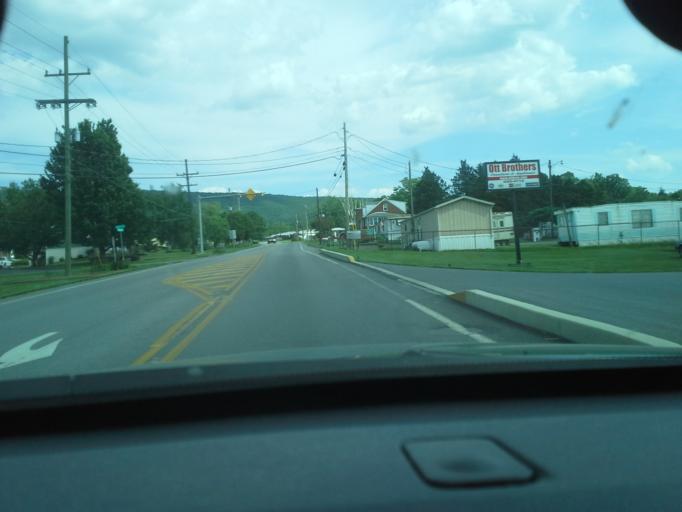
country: US
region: Pennsylvania
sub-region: Fulton County
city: McConnellsburg
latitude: 39.9253
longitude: -77.9852
